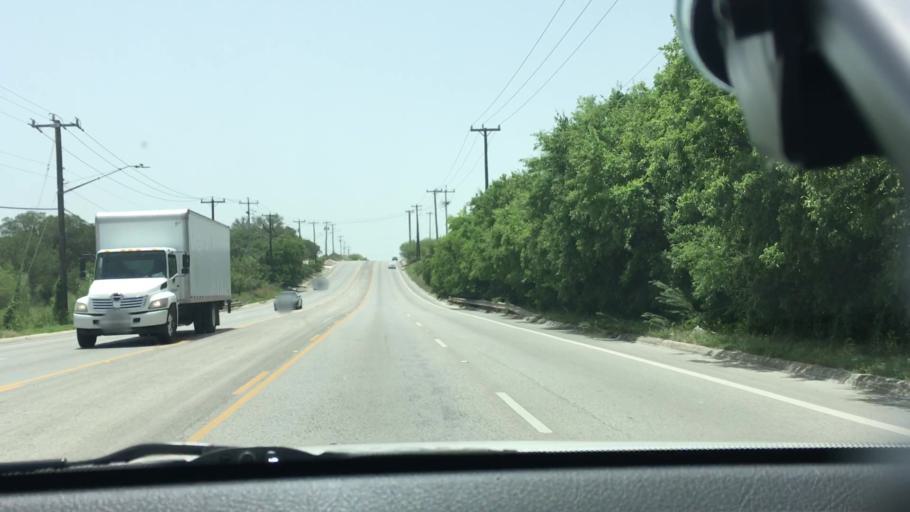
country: US
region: Texas
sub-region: Bexar County
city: Live Oak
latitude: 29.5597
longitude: -98.3511
